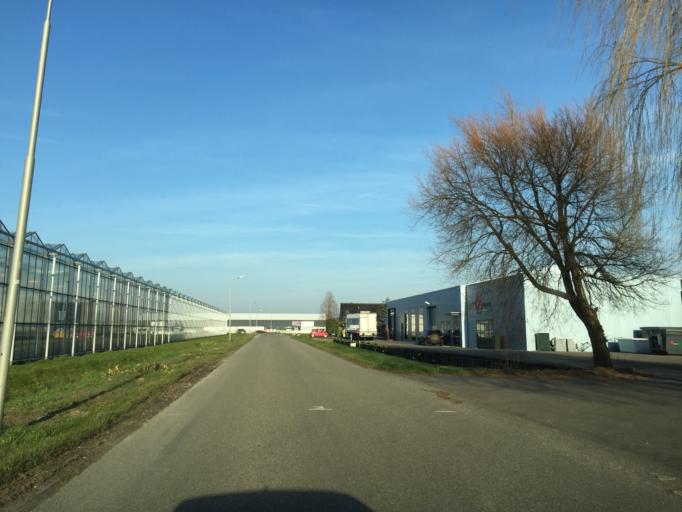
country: NL
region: South Holland
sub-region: Gemeente Pijnacker-Nootdorp
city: Pijnacker
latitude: 52.0143
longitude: 4.3973
